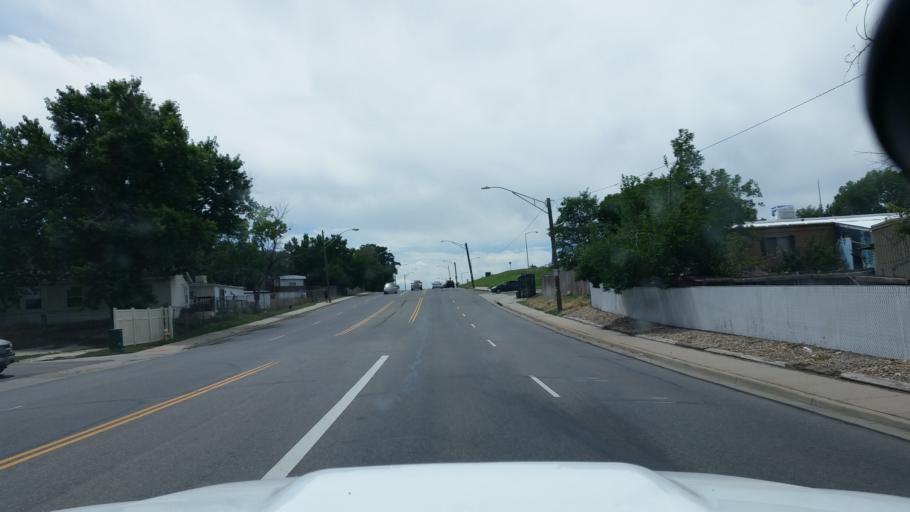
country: US
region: Colorado
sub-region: Adams County
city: Federal Heights
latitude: 39.8607
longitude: -105.0061
